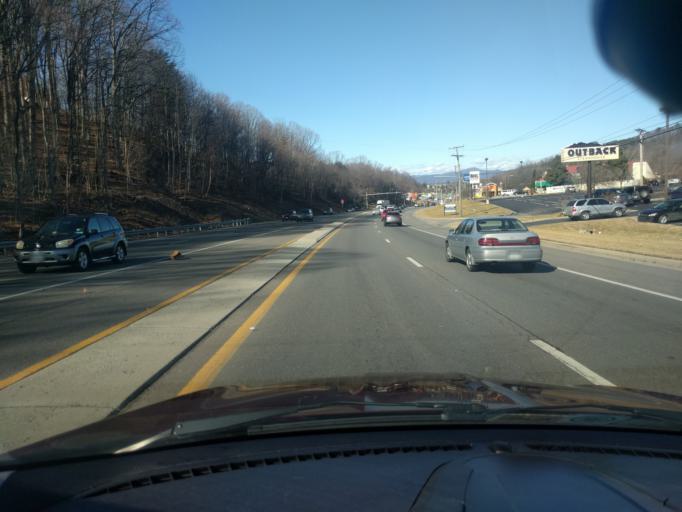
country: US
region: Virginia
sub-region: Roanoke County
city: Narrows
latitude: 37.2204
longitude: -79.9668
